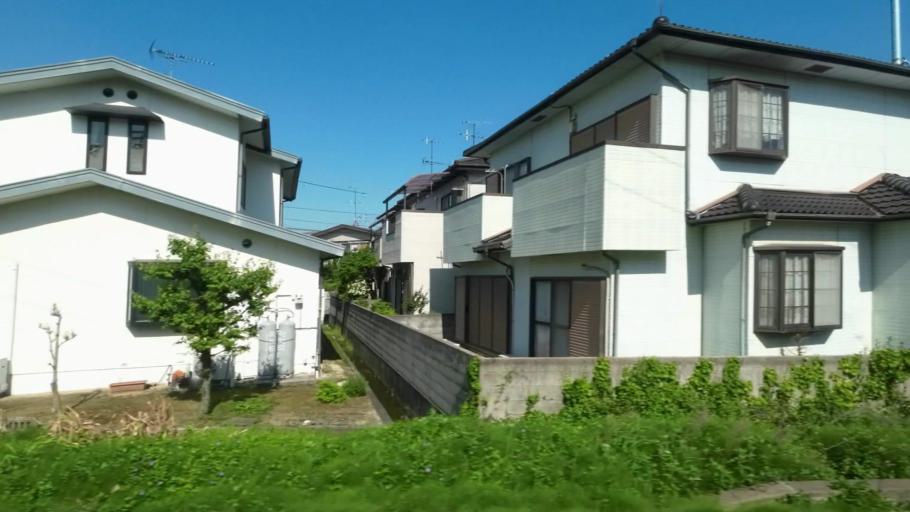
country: JP
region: Kagawa
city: Takamatsu-shi
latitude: 34.3426
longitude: 134.0106
